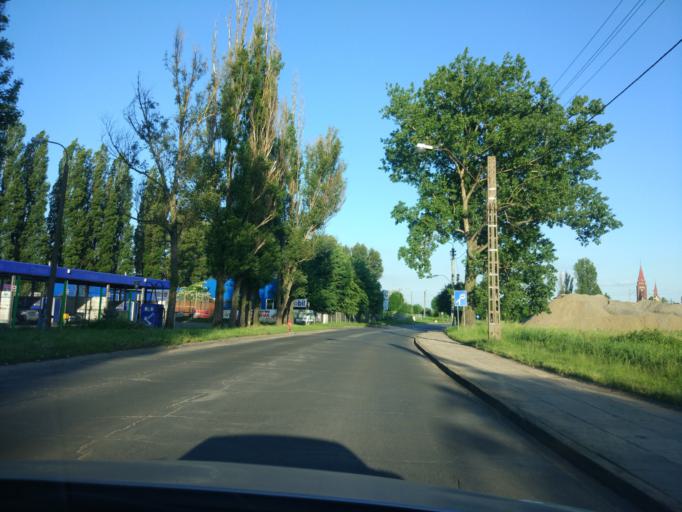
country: PL
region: Lodz Voivodeship
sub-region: Powiat kutnowski
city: Kutno
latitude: 52.2250
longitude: 19.3605
